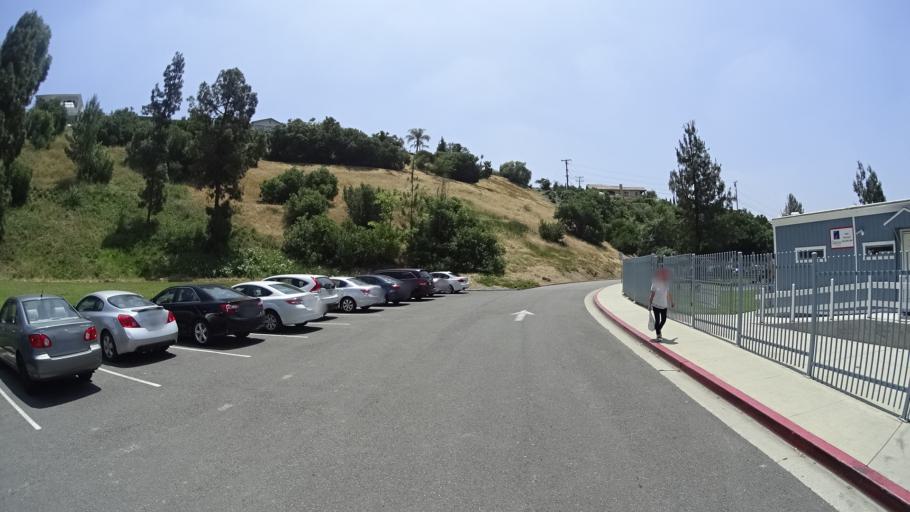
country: US
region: California
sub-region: Los Angeles County
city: Belvedere
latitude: 34.0581
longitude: -118.1534
